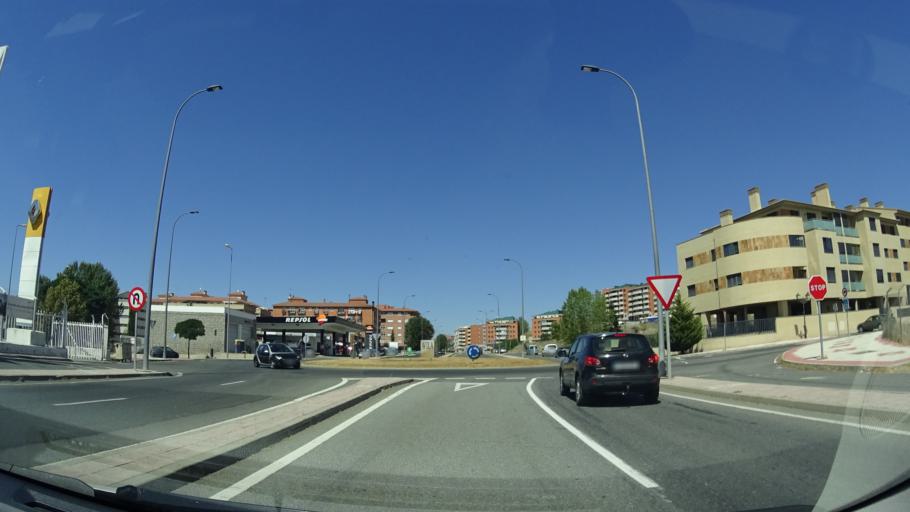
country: ES
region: Castille and Leon
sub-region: Provincia de Avila
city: Avila
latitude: 40.6489
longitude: -4.6722
